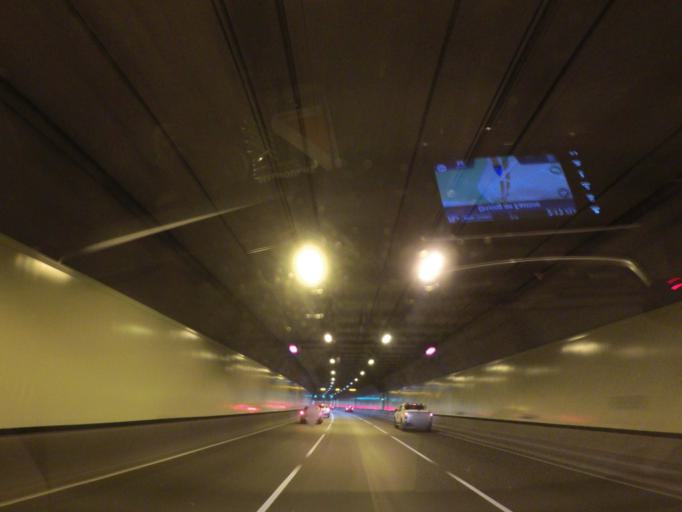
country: AU
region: Victoria
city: Mitcham
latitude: -37.8024
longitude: 145.1983
